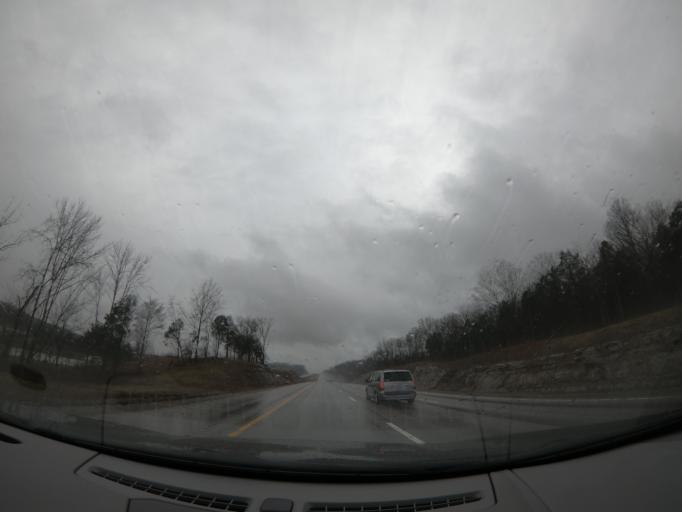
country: US
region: Kentucky
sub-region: Barren County
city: Cave City
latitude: 37.1148
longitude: -86.0255
